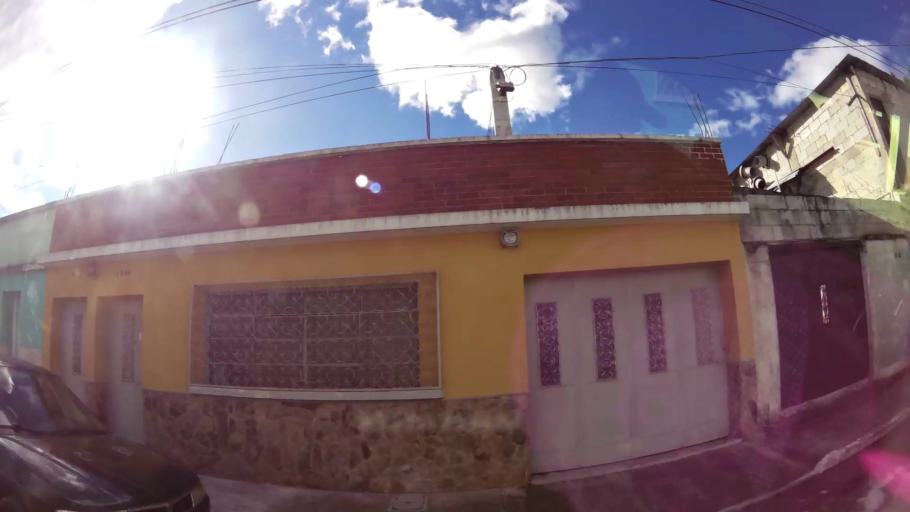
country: GT
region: Guatemala
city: Guatemala City
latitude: 14.6198
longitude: -90.4977
